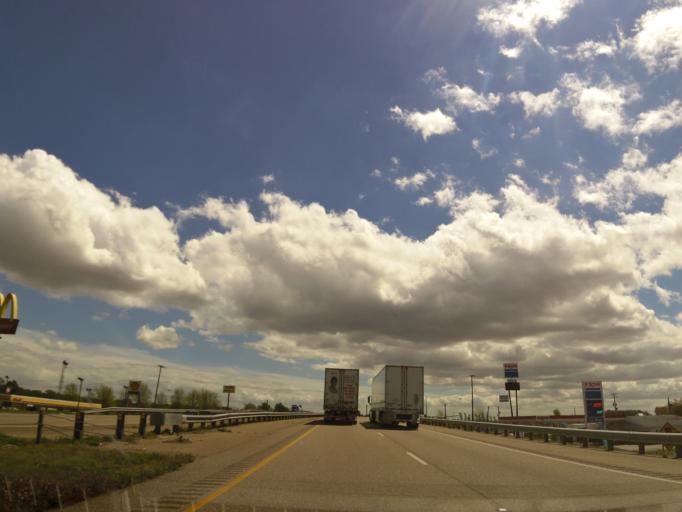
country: US
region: Arkansas
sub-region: Crittenden County
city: Marion
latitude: 35.2139
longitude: -90.2075
